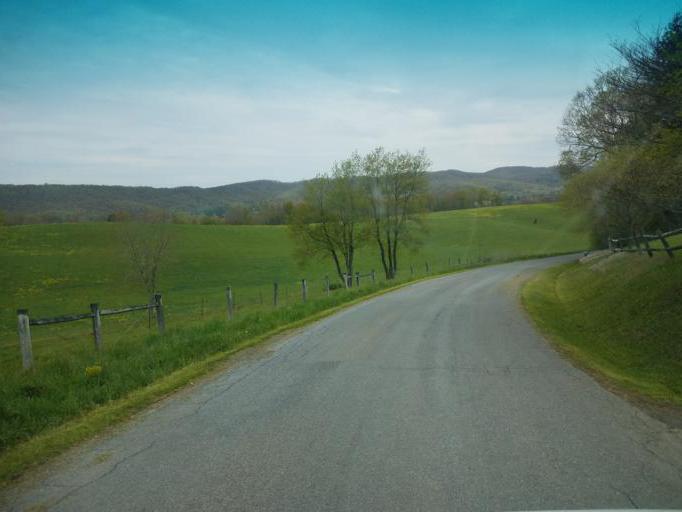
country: US
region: Virginia
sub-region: Smyth County
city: Marion
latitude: 36.7640
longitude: -81.4582
